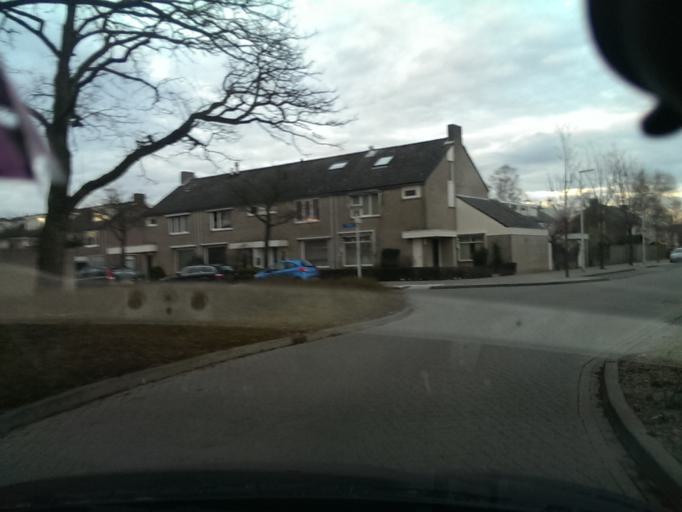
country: NL
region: North Brabant
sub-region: Gemeente Eindhoven
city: Meerhoven
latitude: 51.4244
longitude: 5.4415
